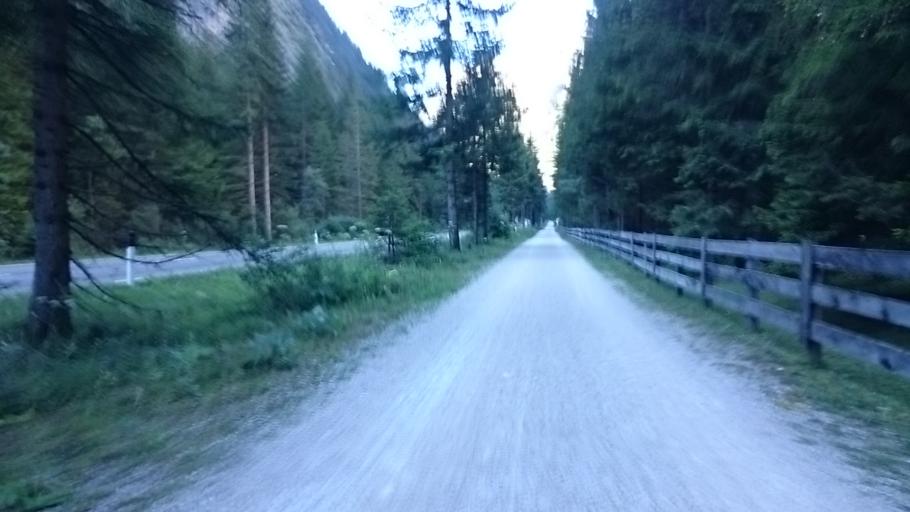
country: IT
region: Trentino-Alto Adige
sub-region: Bolzano
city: Dobbiaco
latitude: 46.6783
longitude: 12.2229
